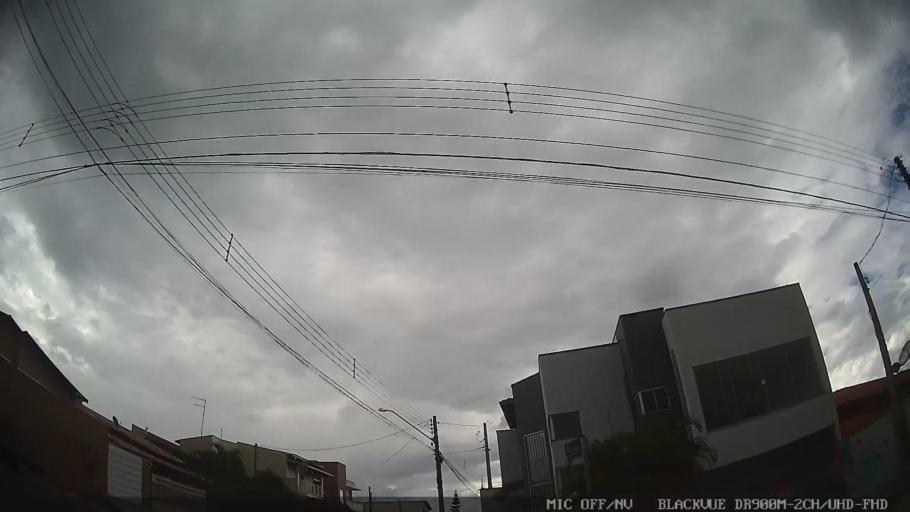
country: BR
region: Sao Paulo
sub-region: Jaguariuna
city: Jaguariuna
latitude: -22.6850
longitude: -46.9870
